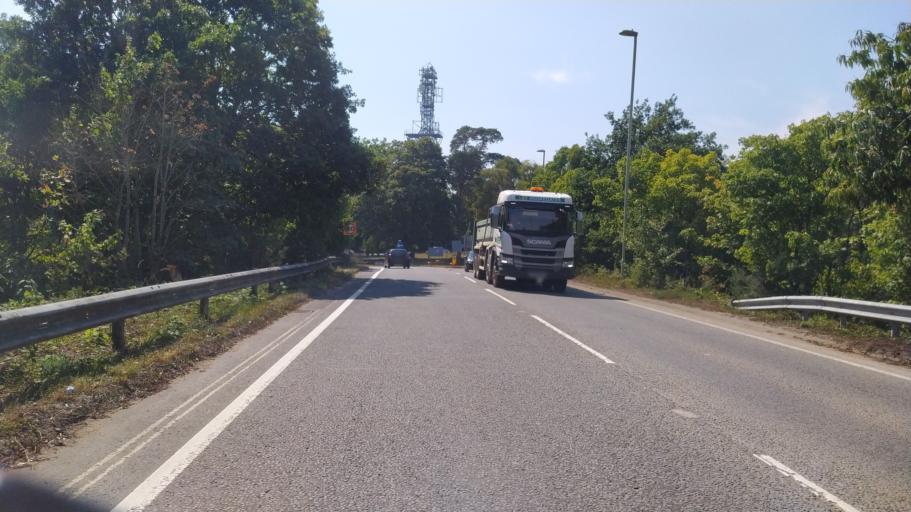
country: GB
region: England
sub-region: Hampshire
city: West End
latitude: 50.9150
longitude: -1.3267
